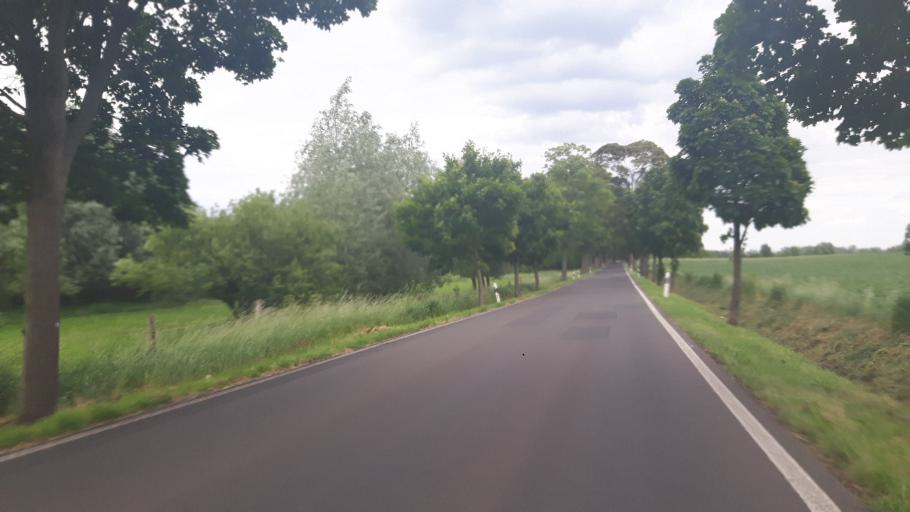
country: DE
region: Brandenburg
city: Eberswalde
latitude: 52.7733
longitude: 13.8398
